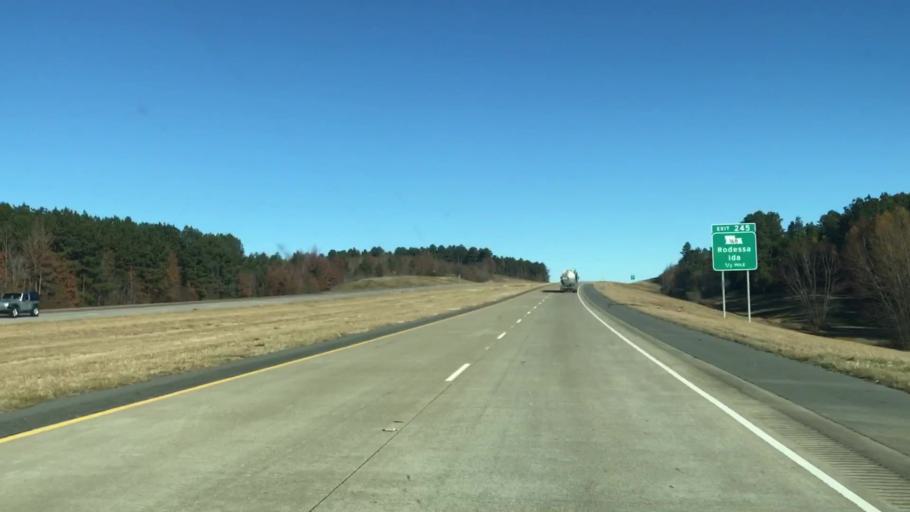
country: US
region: Louisiana
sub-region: Caddo Parish
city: Vivian
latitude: 32.9848
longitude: -93.9105
